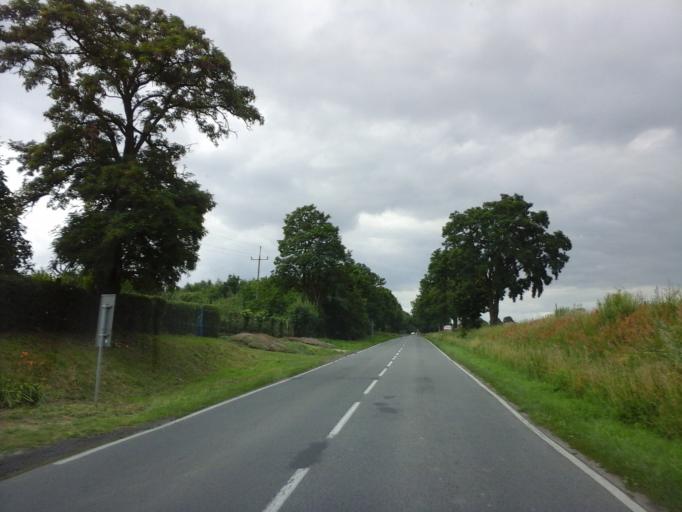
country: PL
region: West Pomeranian Voivodeship
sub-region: Powiat choszczenski
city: Choszczno
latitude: 53.1521
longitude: 15.4389
